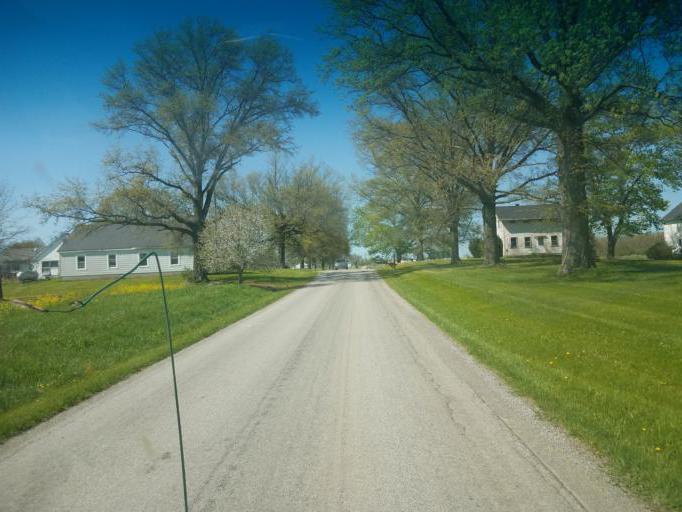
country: US
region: Ohio
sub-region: Medina County
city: Lodi
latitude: 40.9778
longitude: -82.0352
